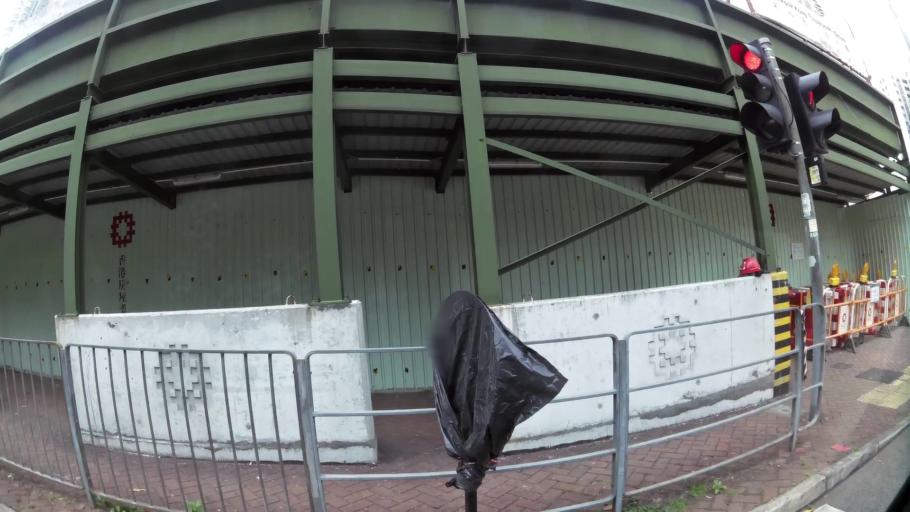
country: HK
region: Kowloon City
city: Kowloon
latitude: 22.3320
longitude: 114.2146
